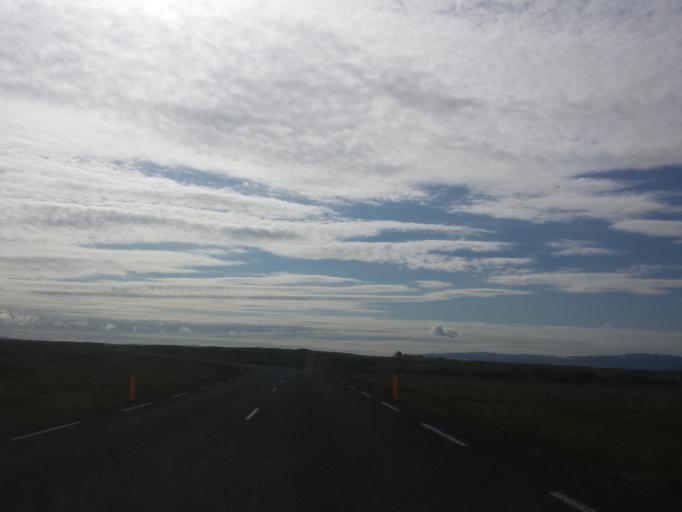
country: IS
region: Northeast
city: Husavik
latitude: 66.0253
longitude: -16.5604
